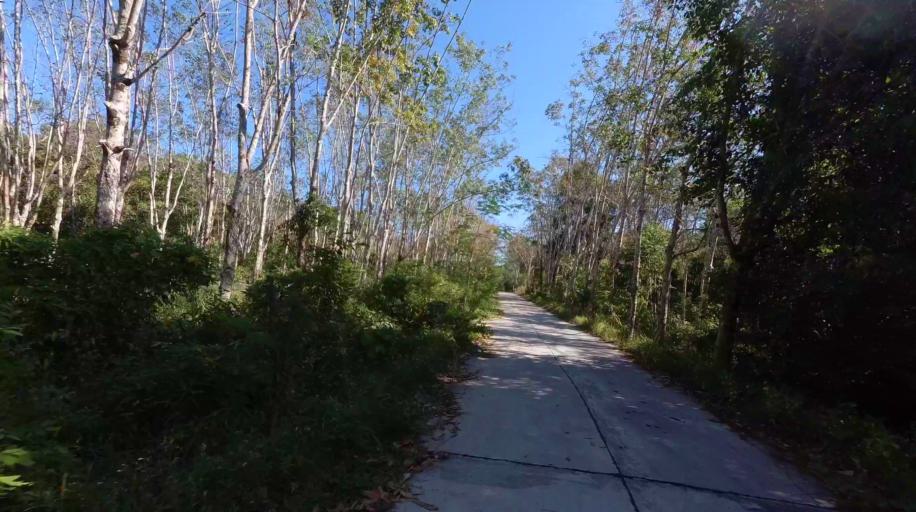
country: TH
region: Trat
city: Ko Kut
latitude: 11.6232
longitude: 102.5531
